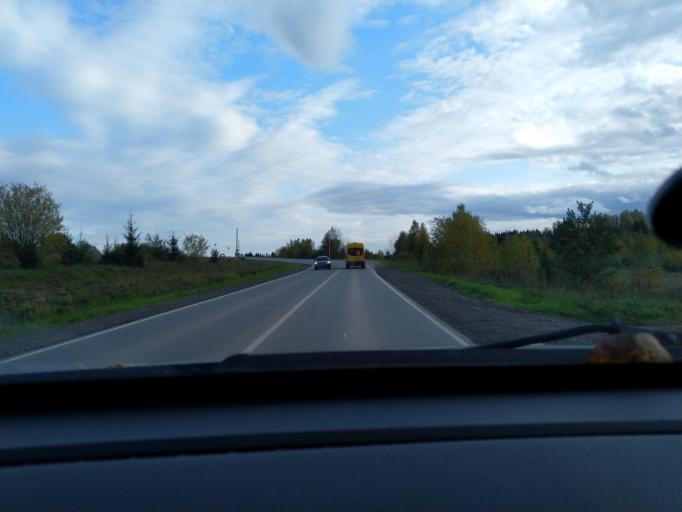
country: RU
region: Perm
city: Polazna
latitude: 58.2763
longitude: 56.4148
